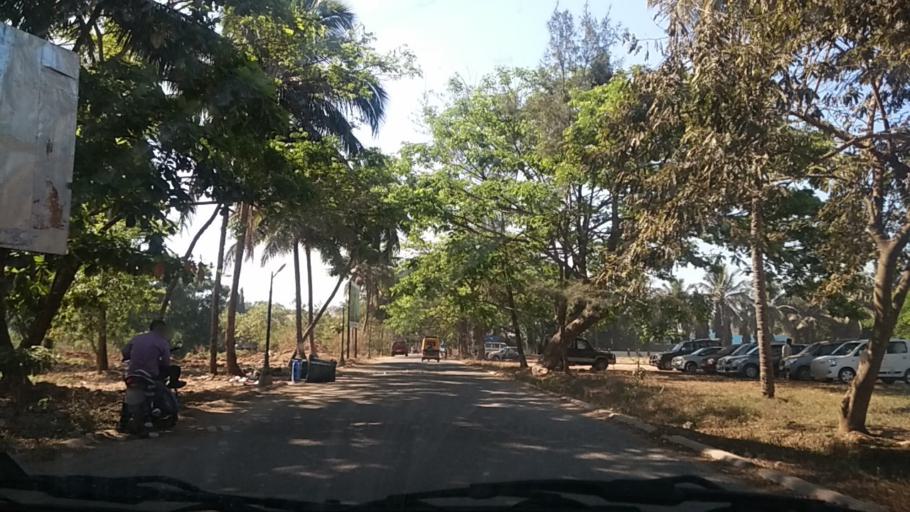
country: IN
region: Goa
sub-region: South Goa
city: Madgaon
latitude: 15.2669
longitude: 73.9718
